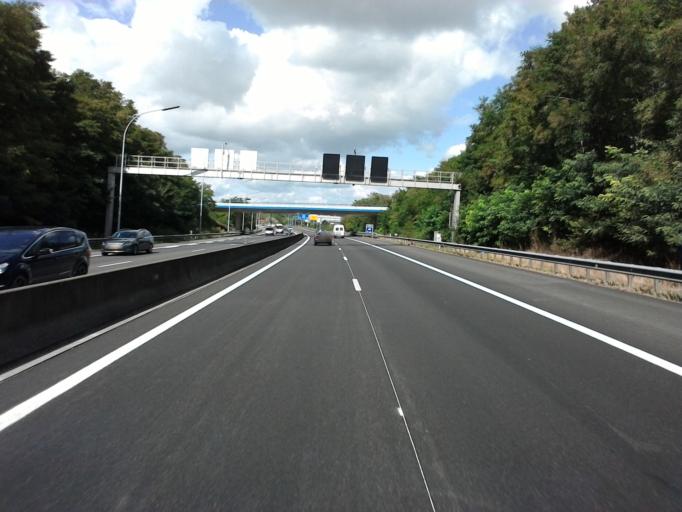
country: LU
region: Luxembourg
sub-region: Canton de Capellen
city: Mamer
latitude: 49.6382
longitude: 6.0188
